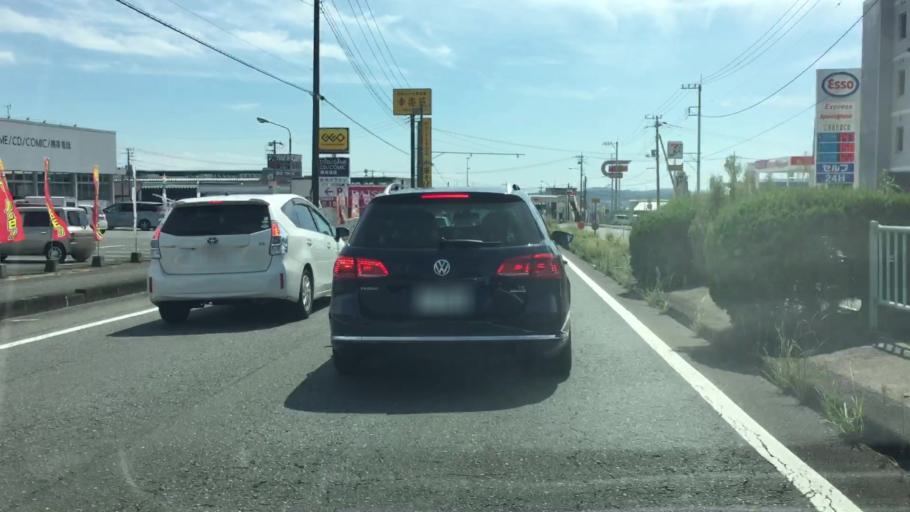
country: JP
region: Shizuoka
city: Fujinomiya
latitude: 35.2342
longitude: 138.6208
